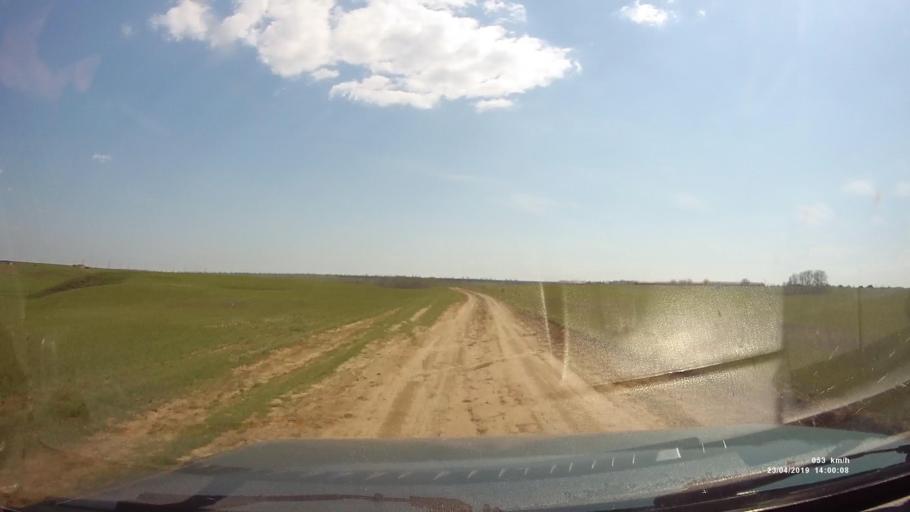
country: RU
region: Rostov
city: Remontnoye
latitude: 46.5614
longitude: 42.9470
